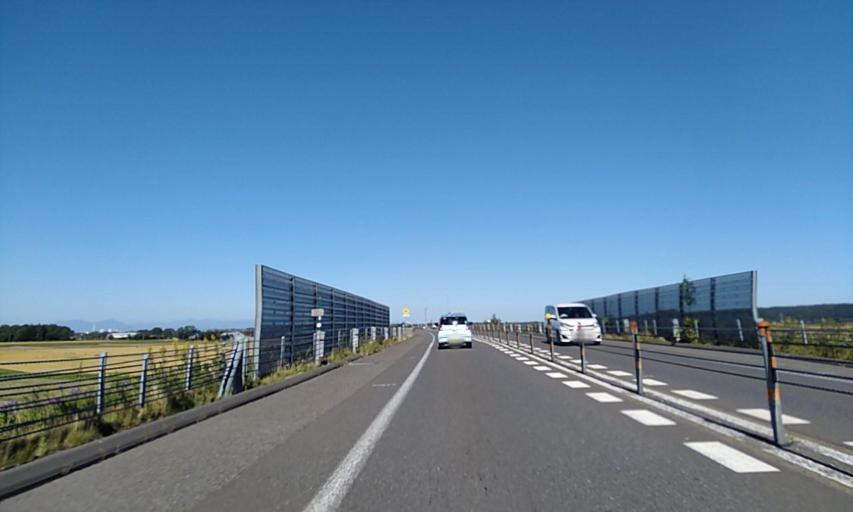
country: JP
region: Hokkaido
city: Tomakomai
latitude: 42.5728
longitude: 141.9726
